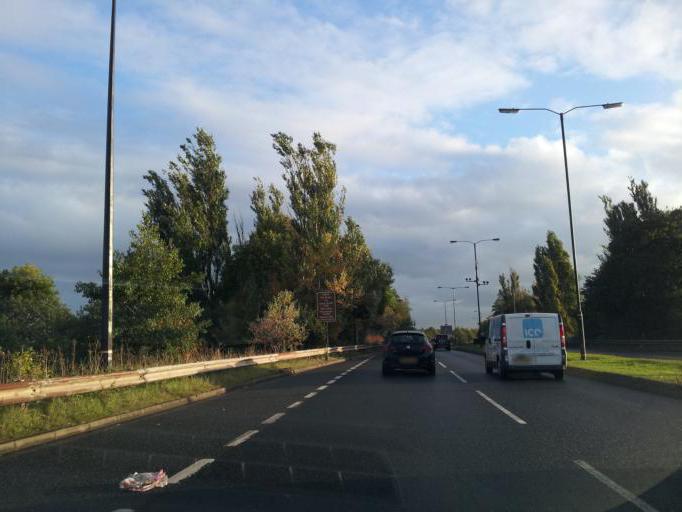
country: GB
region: England
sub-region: City and Borough of Salford
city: Eccles
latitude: 53.4652
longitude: -2.3318
